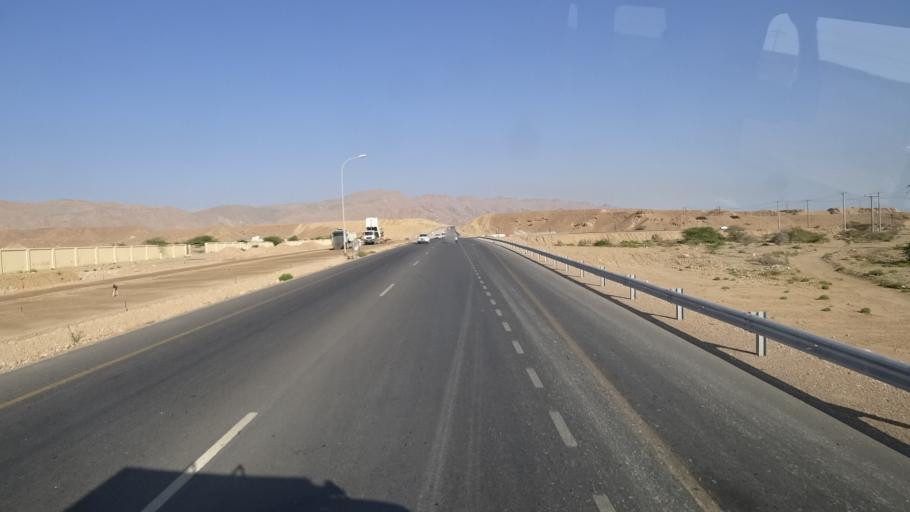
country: OM
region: Ash Sharqiyah
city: Sur
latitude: 22.5778
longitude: 59.4587
